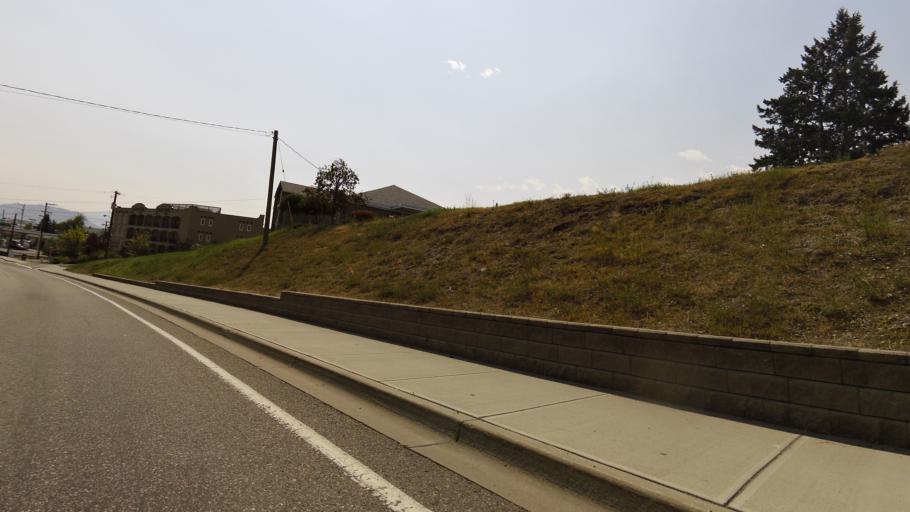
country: CA
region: British Columbia
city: Osoyoos
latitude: 49.0337
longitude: -119.4728
